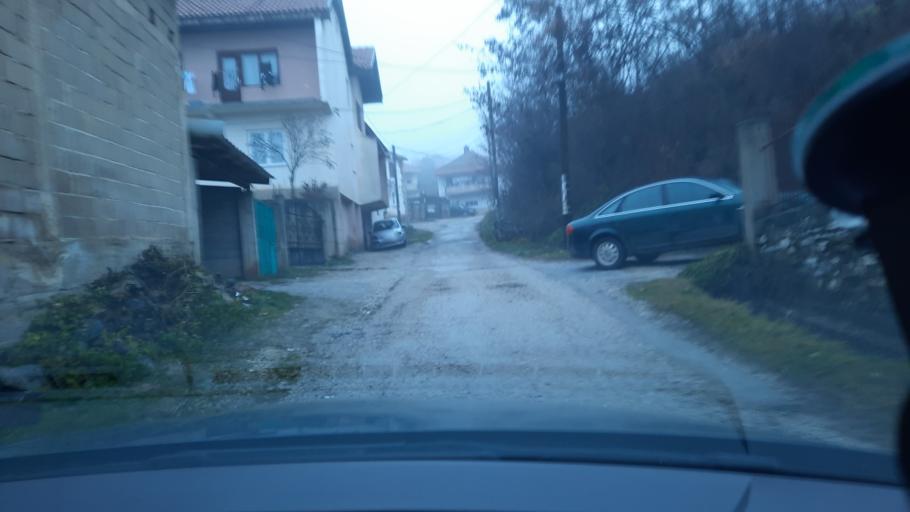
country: MK
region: Vrapciste
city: Vrapciste
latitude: 41.8403
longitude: 20.8791
